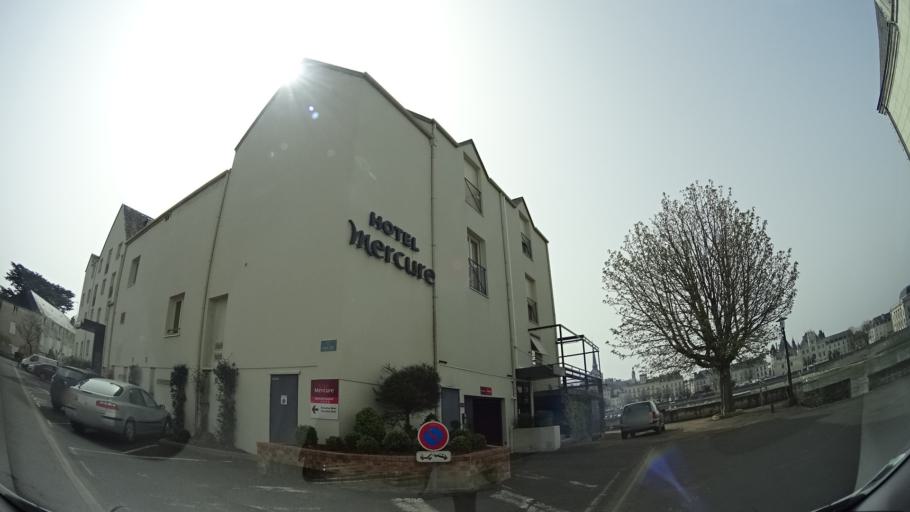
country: FR
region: Pays de la Loire
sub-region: Departement de Maine-et-Loire
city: Saumur
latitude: 47.2623
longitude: -0.0720
